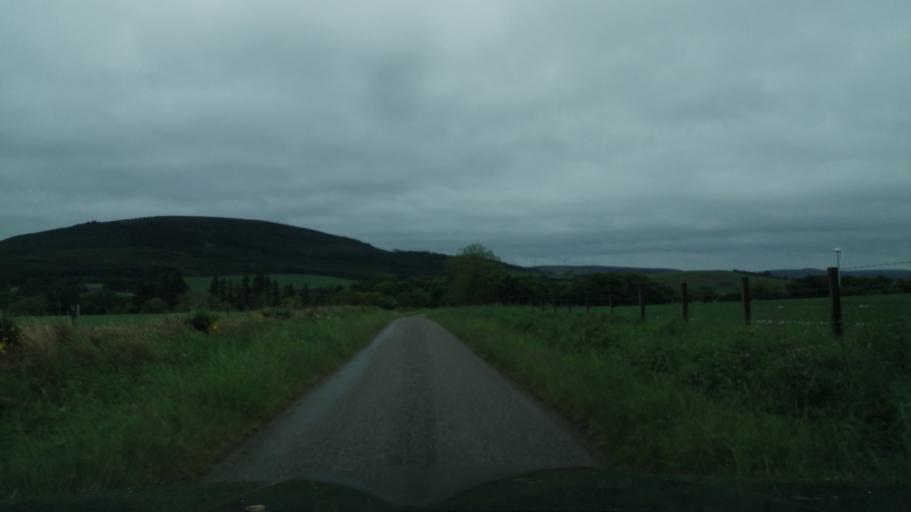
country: GB
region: Scotland
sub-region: Moray
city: Keith
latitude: 57.5548
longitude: -2.8689
